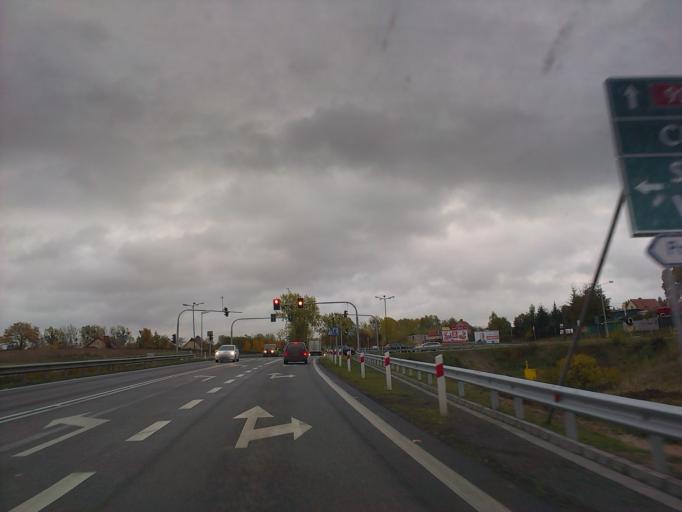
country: PL
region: Kujawsko-Pomorskie
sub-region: Powiat chelminski
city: Chelmno
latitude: 53.3527
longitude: 18.4504
